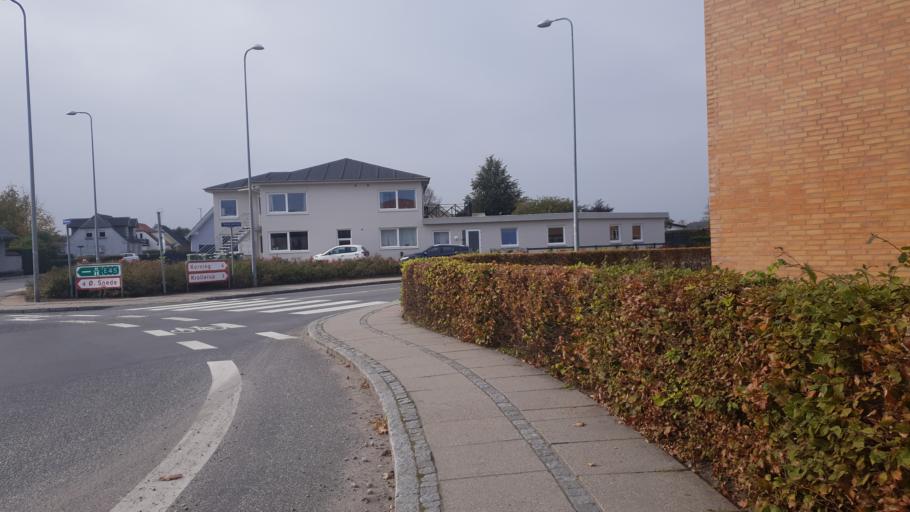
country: DK
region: Central Jutland
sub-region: Hedensted Kommune
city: Hedensted
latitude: 55.8039
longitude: 9.6921
